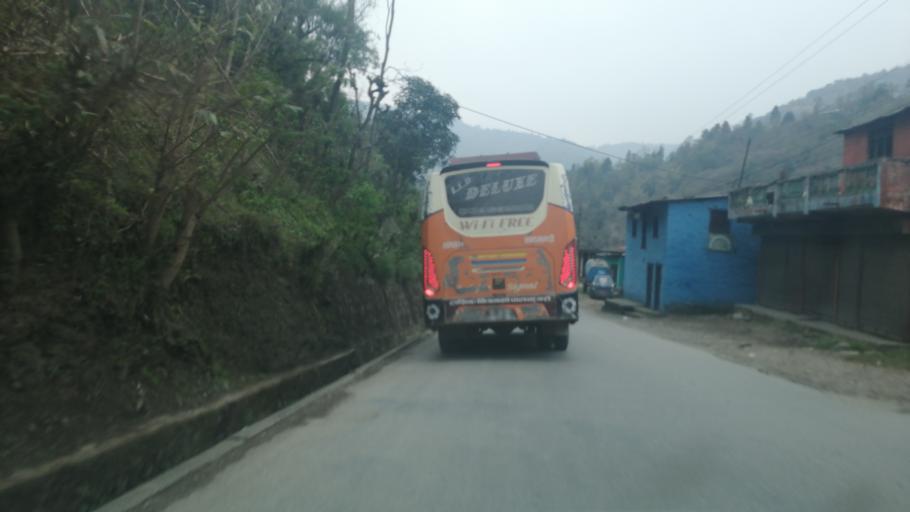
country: NP
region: Western Region
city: Tansen
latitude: 27.8121
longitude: 83.5235
